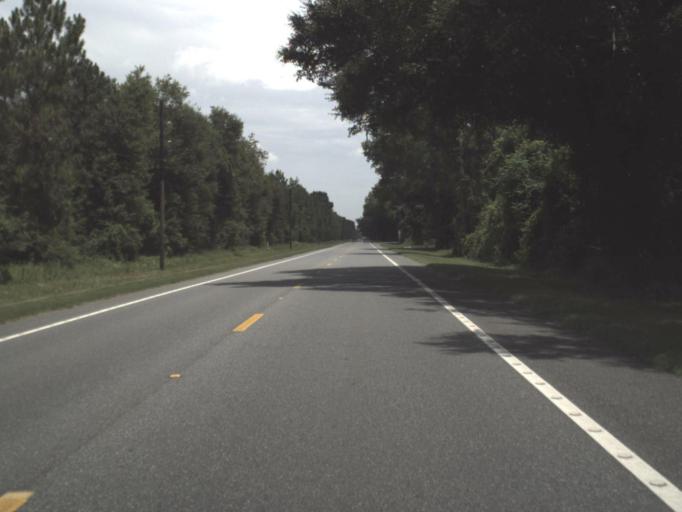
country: US
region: Florida
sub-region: Lafayette County
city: Mayo
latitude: 30.0185
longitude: -82.9382
